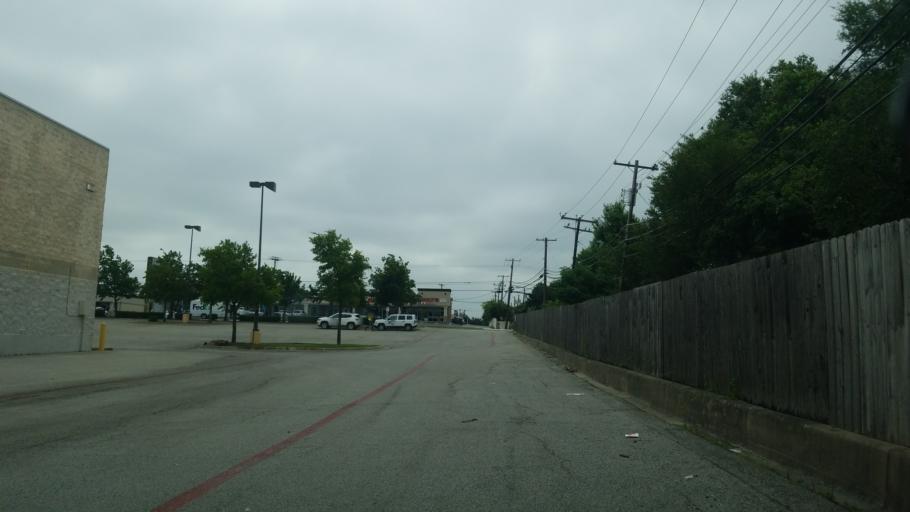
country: US
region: Texas
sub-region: Dallas County
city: Farmers Branch
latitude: 32.9081
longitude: -96.8572
